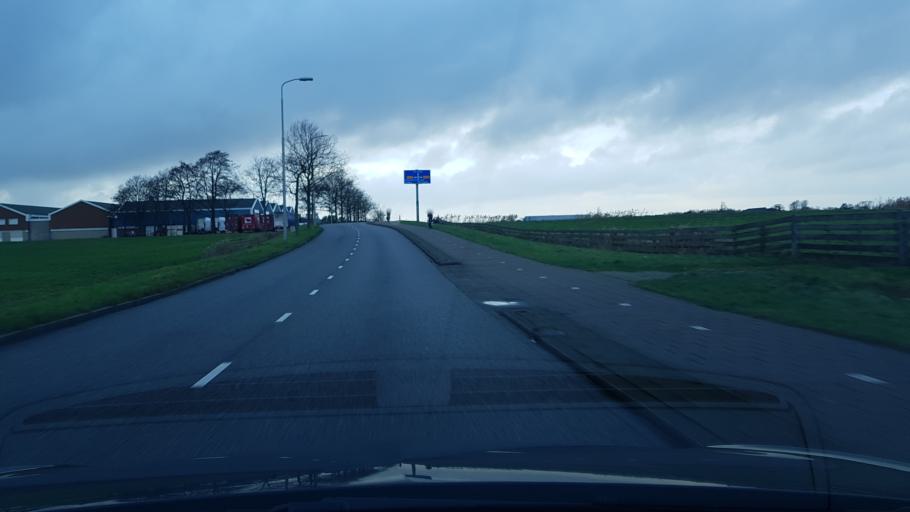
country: NL
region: South Holland
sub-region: Gemeente Lisse
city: Lisse
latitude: 52.2422
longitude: 4.5466
